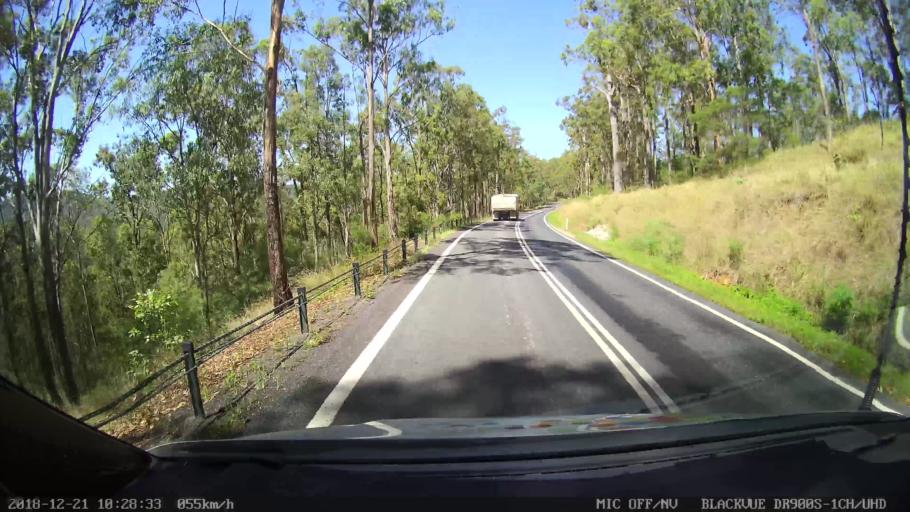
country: AU
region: New South Wales
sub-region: Clarence Valley
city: South Grafton
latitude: -29.6315
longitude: 152.7337
